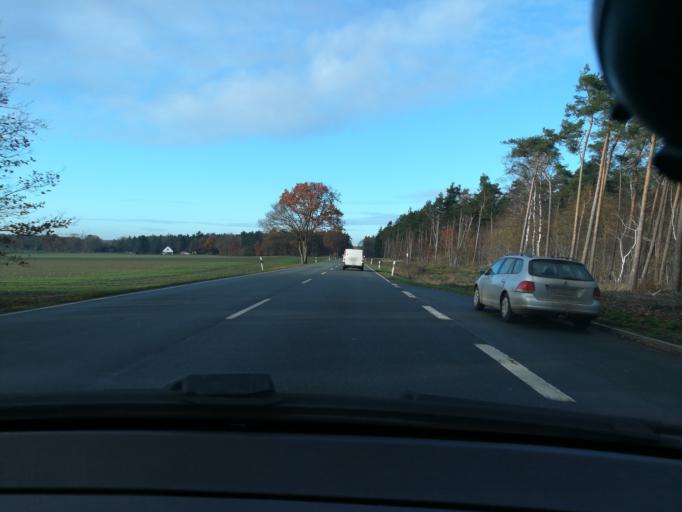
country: DE
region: Lower Saxony
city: Uchte
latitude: 52.5315
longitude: 8.8802
